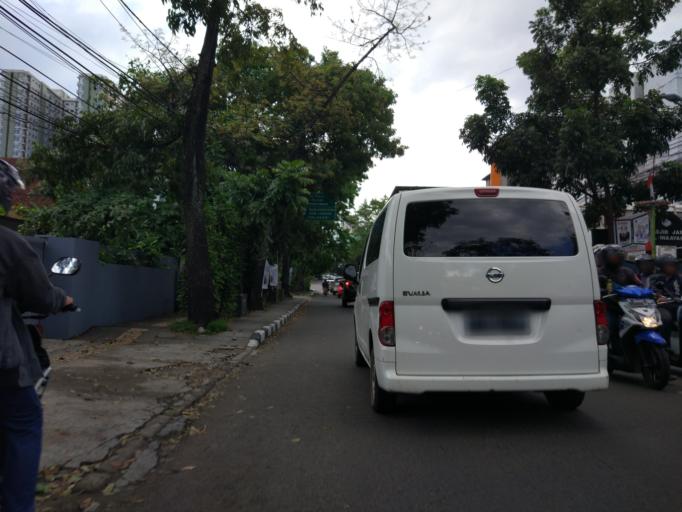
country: ID
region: West Java
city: Bandung
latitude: -6.9229
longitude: 107.6210
